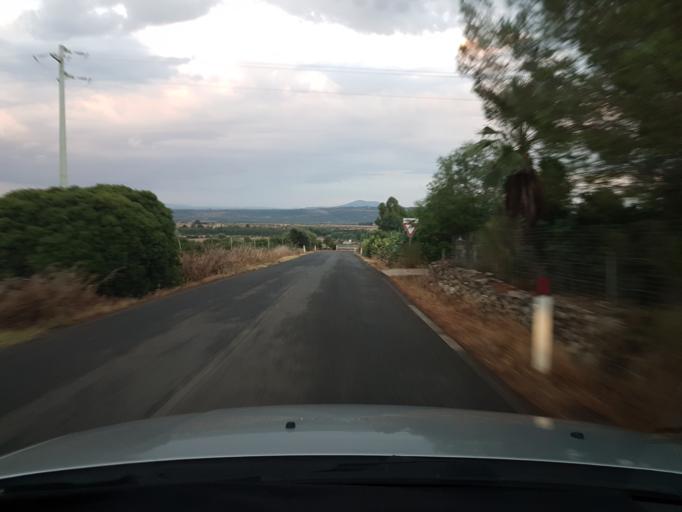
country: IT
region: Sardinia
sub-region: Provincia di Oristano
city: Milis
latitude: 40.0573
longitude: 8.6358
